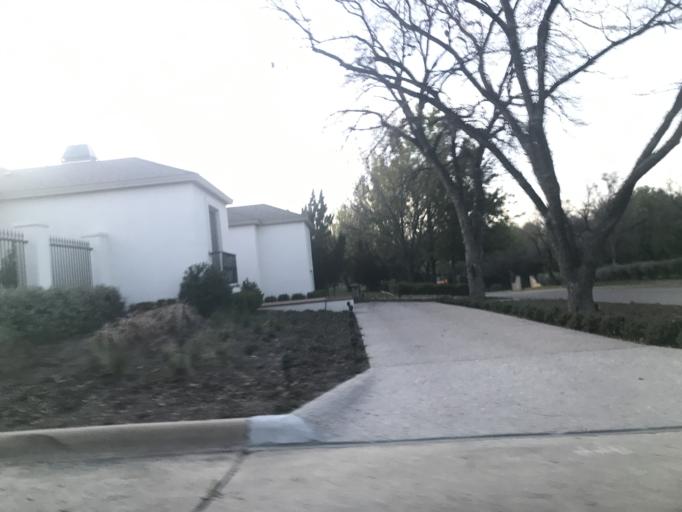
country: US
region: Texas
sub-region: Tom Green County
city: San Angelo
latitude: 31.4552
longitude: -100.4496
